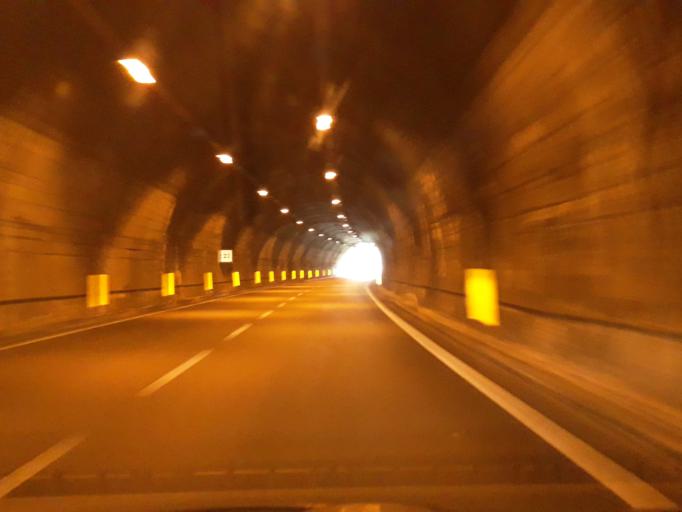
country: IT
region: Sicily
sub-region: Palermo
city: Trabia
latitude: 37.9913
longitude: 13.6534
